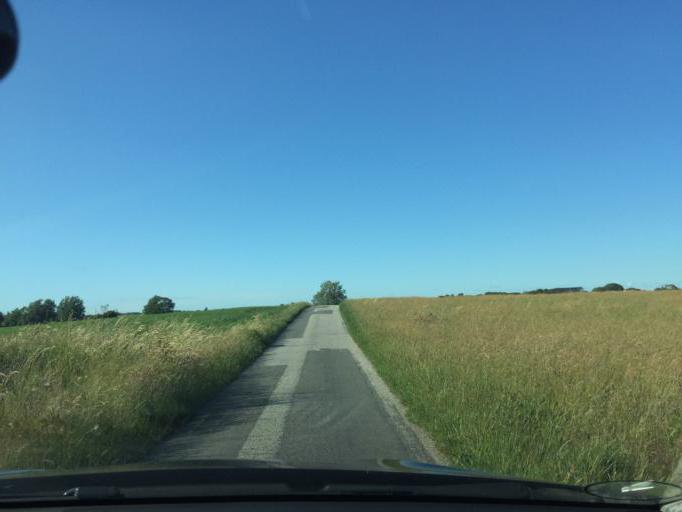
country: DK
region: Zealand
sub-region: Slagelse Kommune
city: Skaelskor
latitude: 55.2046
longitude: 11.1819
